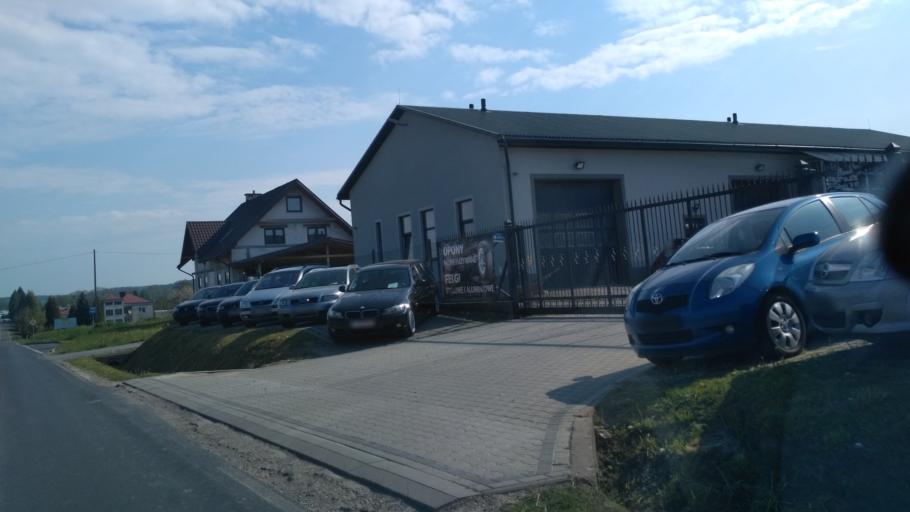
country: PL
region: Subcarpathian Voivodeship
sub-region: Powiat rzeszowski
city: Dynow
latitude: 49.8277
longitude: 22.2337
